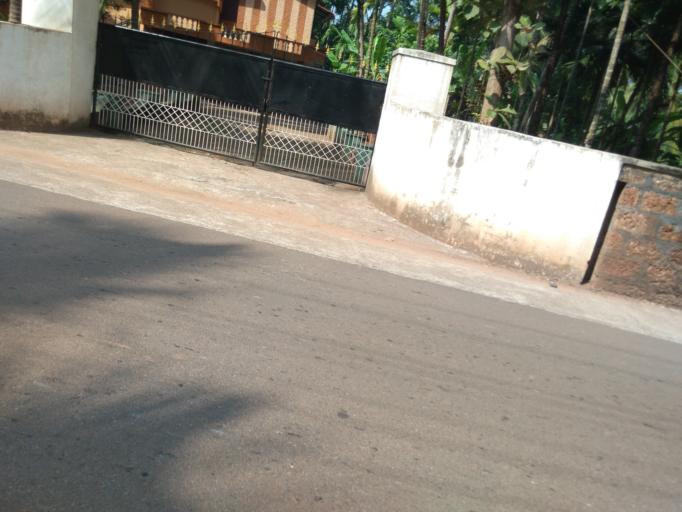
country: IN
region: Kerala
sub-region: Kozhikode
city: Kunnamangalam
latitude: 11.2889
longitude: 75.8358
